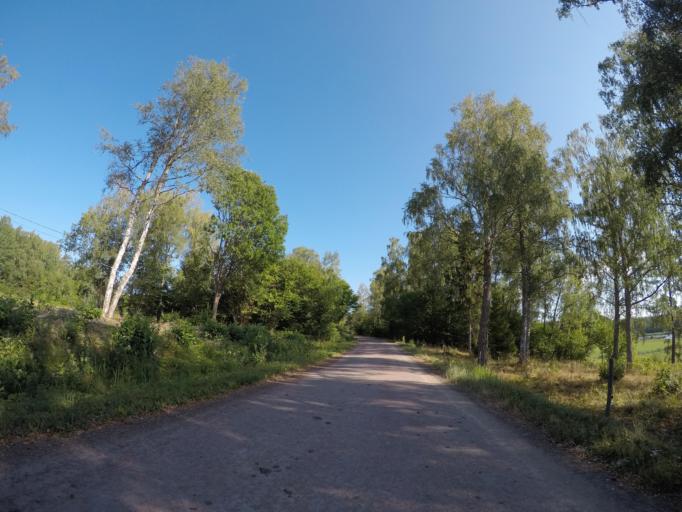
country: AX
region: Alands landsbygd
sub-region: Finstroem
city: Finstroem
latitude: 60.2476
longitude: 19.9217
